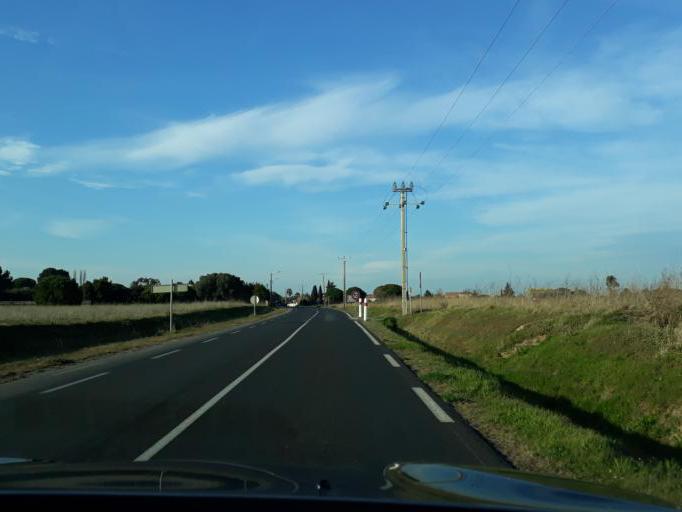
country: FR
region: Languedoc-Roussillon
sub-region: Departement de l'Herault
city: Marseillan
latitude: 43.3316
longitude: 3.5252
